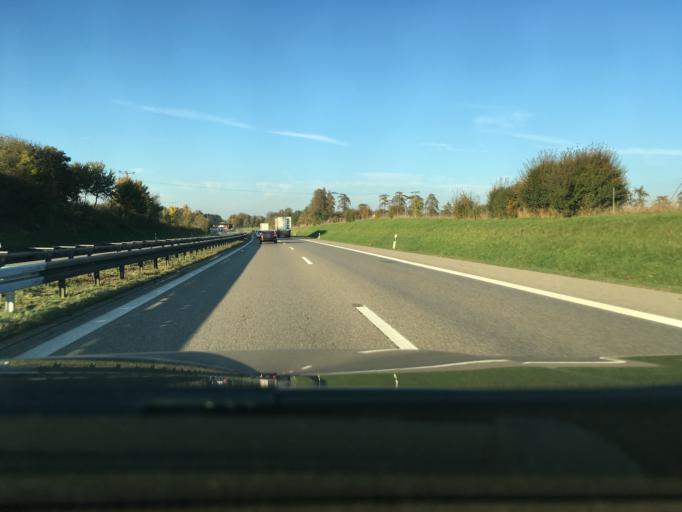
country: DE
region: Baden-Wuerttemberg
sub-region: Tuebingen Region
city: Aitrach
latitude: 47.9473
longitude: 10.1037
